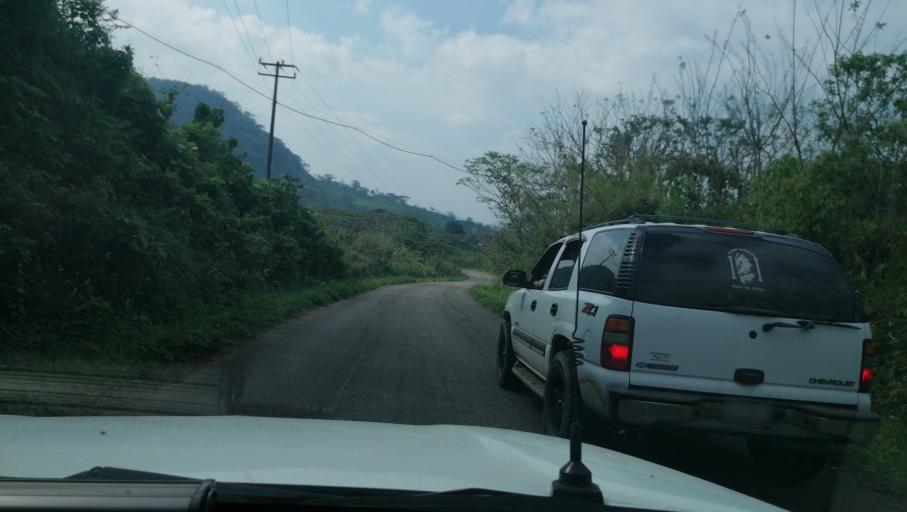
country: MX
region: Chiapas
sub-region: Francisco Leon
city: San Miguel la Sardina
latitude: 17.2290
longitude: -93.3486
